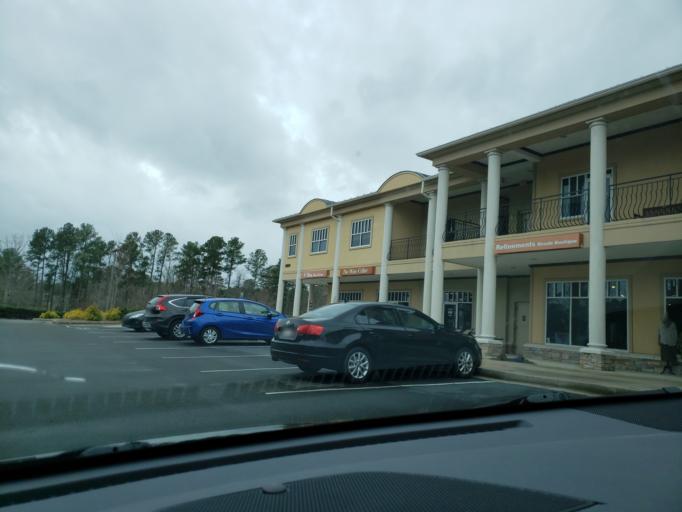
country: US
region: North Carolina
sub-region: Durham County
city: Durham
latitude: 35.9199
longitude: -78.9299
